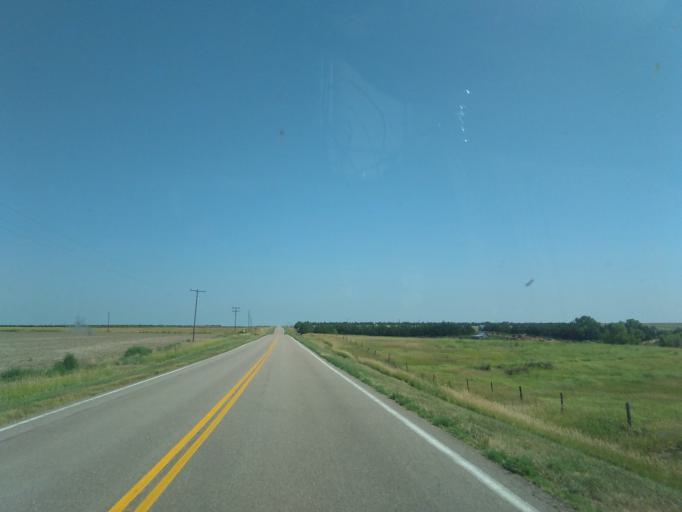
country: US
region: Nebraska
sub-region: Dundy County
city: Benkelman
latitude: 39.8990
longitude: -101.5411
